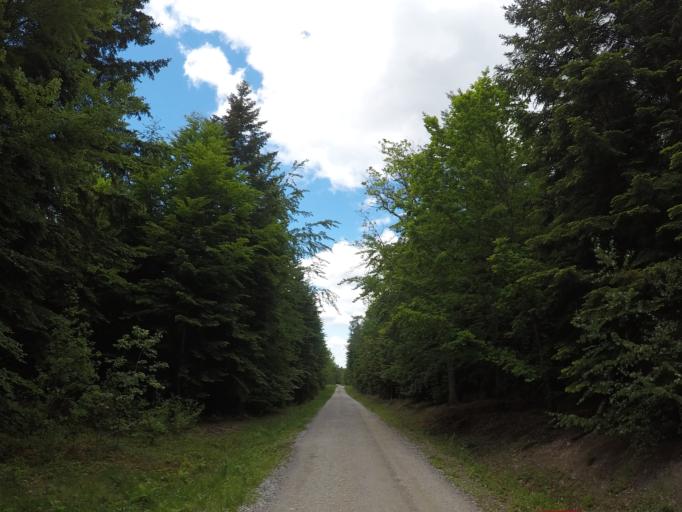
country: PL
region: Swietokrzyskie
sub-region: Powiat kielecki
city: Kielce
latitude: 50.9147
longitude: 20.6490
